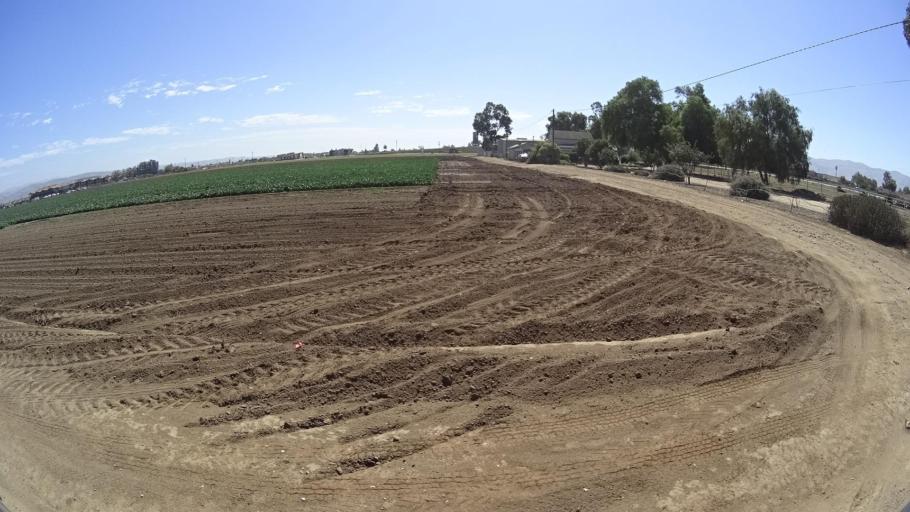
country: US
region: California
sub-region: Monterey County
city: Greenfield
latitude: 36.3336
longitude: -121.2453
